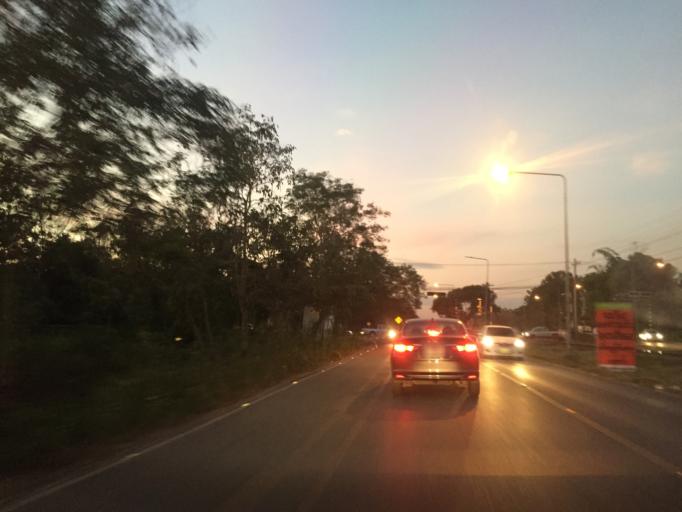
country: TH
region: Chiang Mai
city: Saraphi
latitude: 18.7154
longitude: 99.0394
